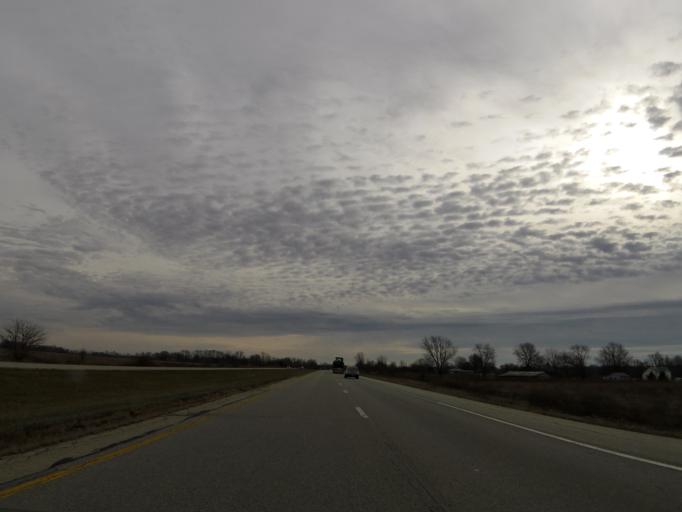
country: US
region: Indiana
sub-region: Hendricks County
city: Pittsboro
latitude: 39.9392
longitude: -86.6121
